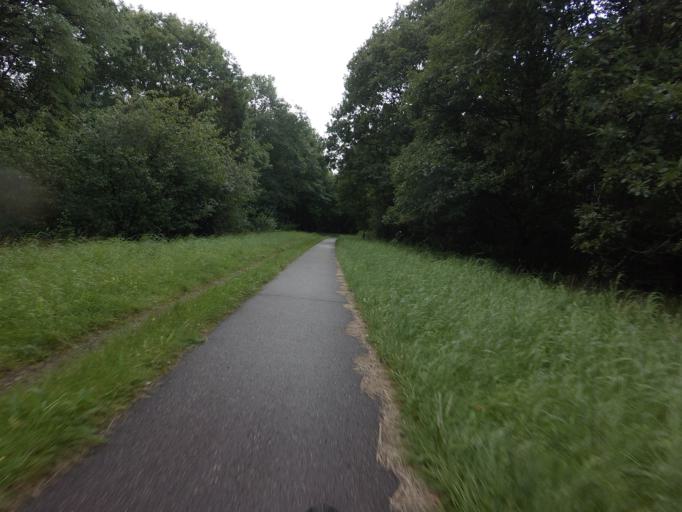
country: DK
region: Central Jutland
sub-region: Silkeborg Kommune
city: Silkeborg
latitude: 56.1234
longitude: 9.4235
